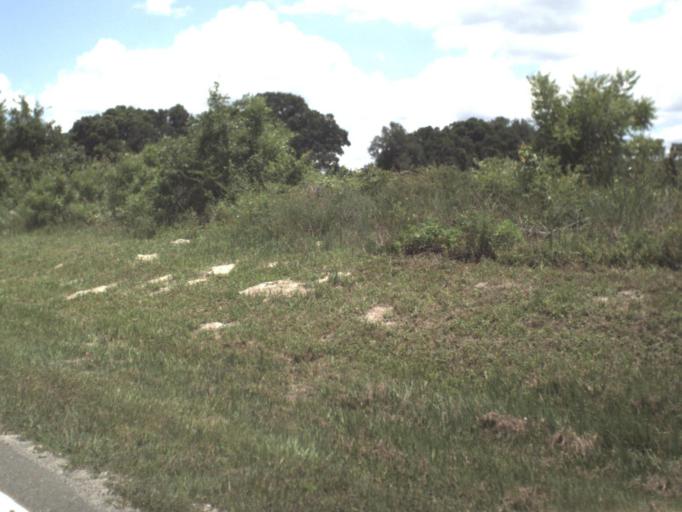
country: US
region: Florida
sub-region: Clay County
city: Keystone Heights
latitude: 29.7530
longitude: -82.0565
